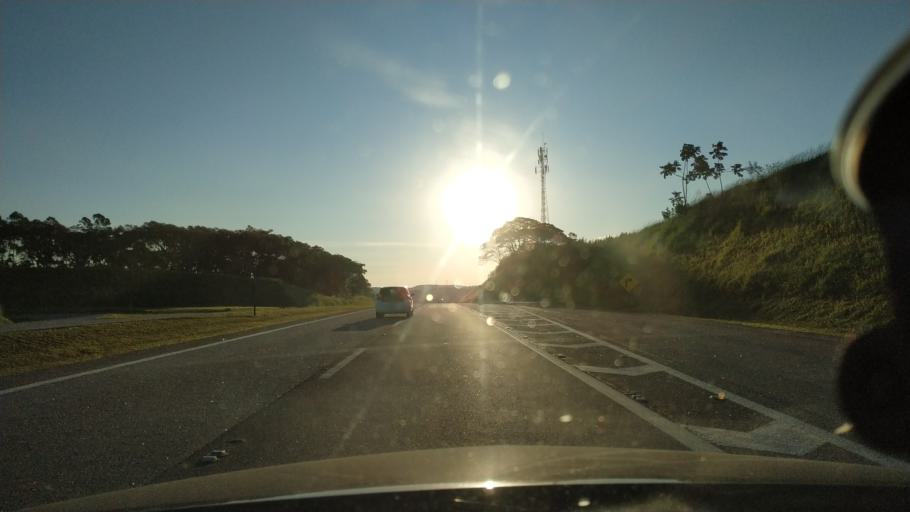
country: BR
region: Sao Paulo
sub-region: Sao Jose Dos Campos
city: Sao Jose dos Campos
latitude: -23.2674
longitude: -45.8217
